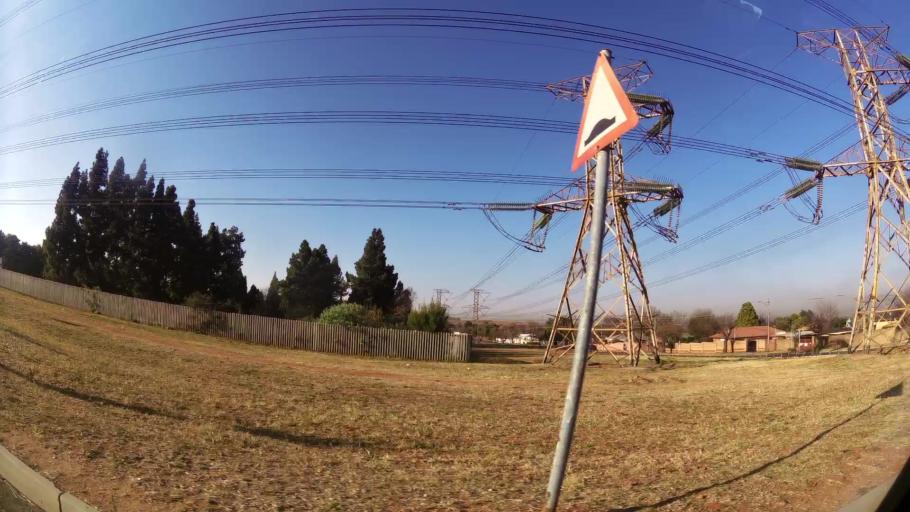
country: ZA
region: Gauteng
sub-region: Ekurhuleni Metropolitan Municipality
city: Germiston
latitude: -26.1939
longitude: 28.1411
